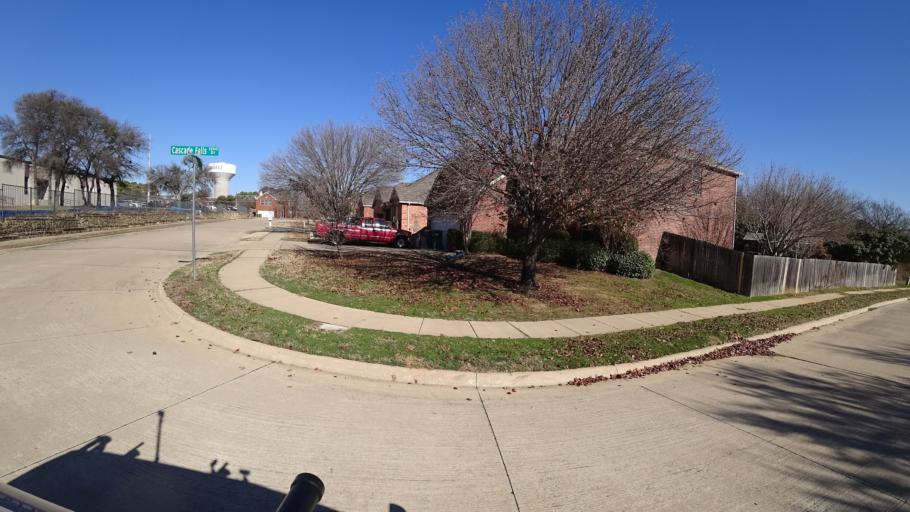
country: US
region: Texas
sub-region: Denton County
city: Lewisville
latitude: 33.0262
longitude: -97.0232
